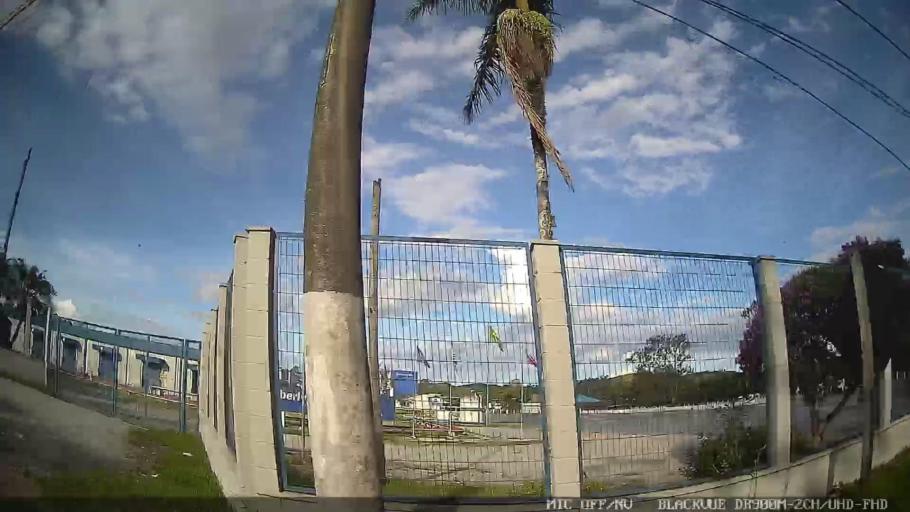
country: BR
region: Sao Paulo
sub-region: Mogi das Cruzes
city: Mogi das Cruzes
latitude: -23.5417
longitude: -46.1539
